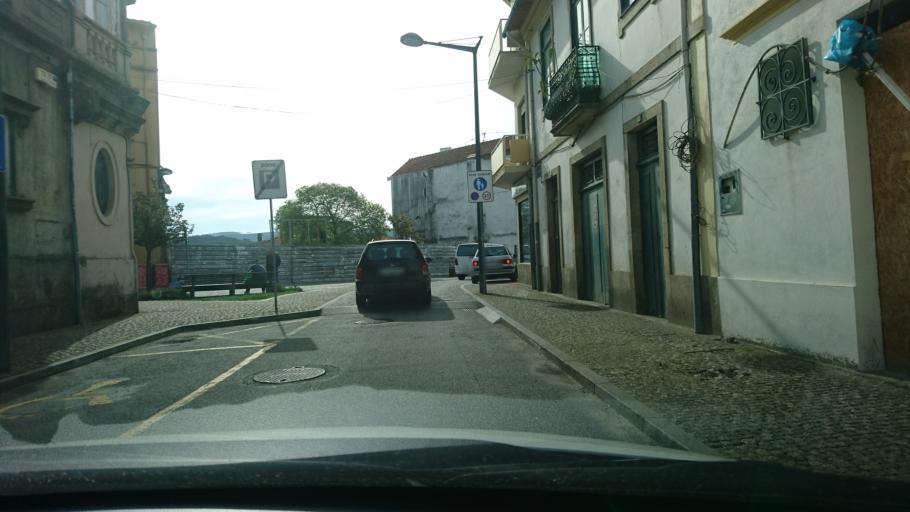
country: PT
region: Aveiro
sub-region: Oliveira de Azemeis
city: Oliveira de Azemeis
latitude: 40.8377
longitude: -8.4784
